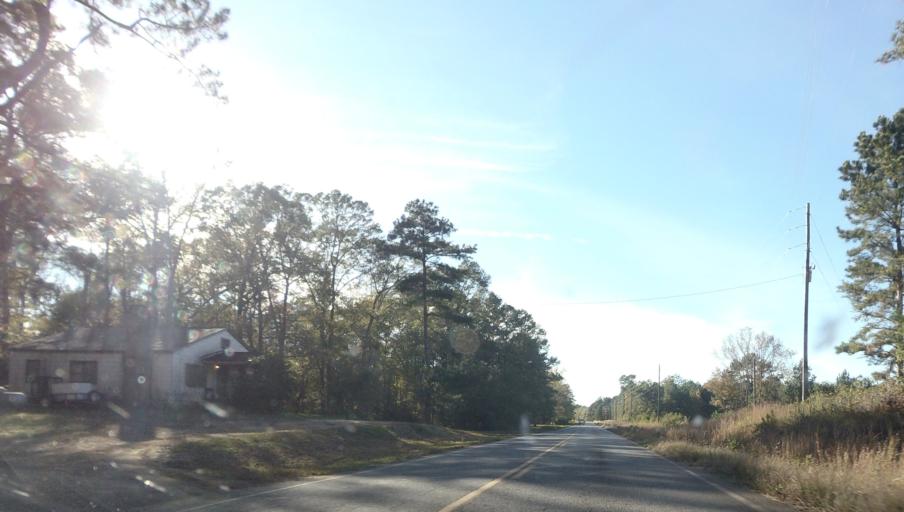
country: US
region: Georgia
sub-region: Talbot County
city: Sardis
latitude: 32.6899
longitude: -84.6811
